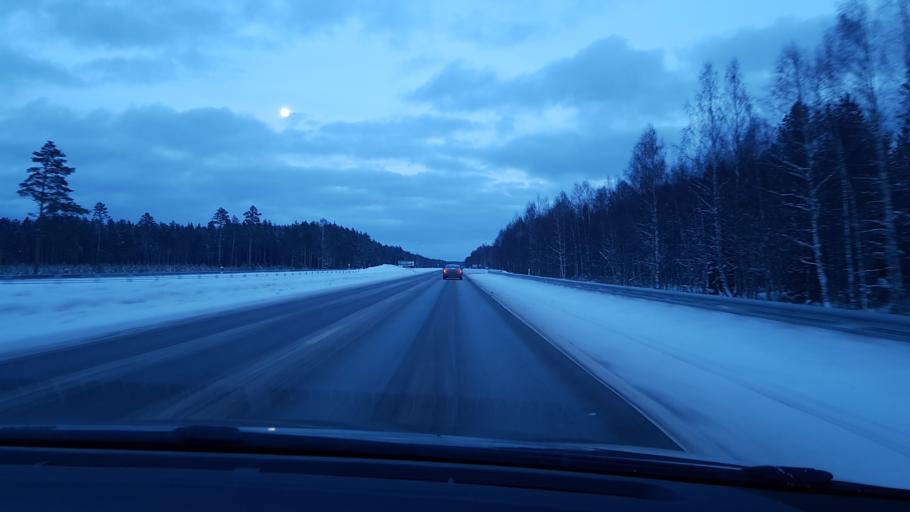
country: EE
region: Harju
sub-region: Kuusalu vald
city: Kuusalu
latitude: 59.4598
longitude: 25.5809
